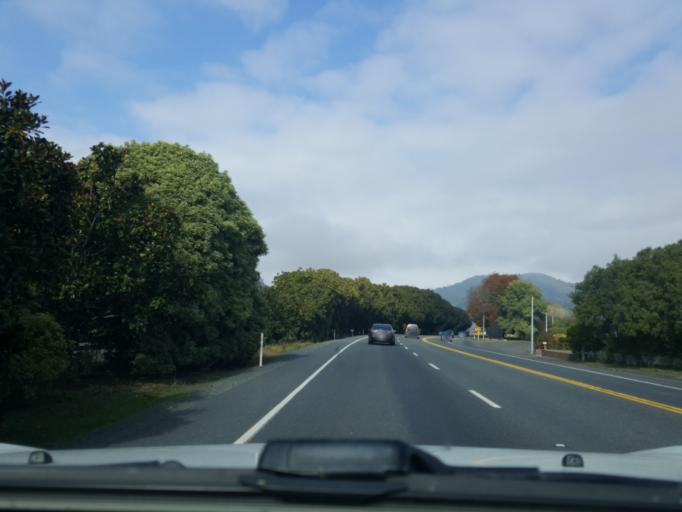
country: NZ
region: Waikato
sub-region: Waikato District
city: Ngaruawahia
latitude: -37.5825
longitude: 175.1594
